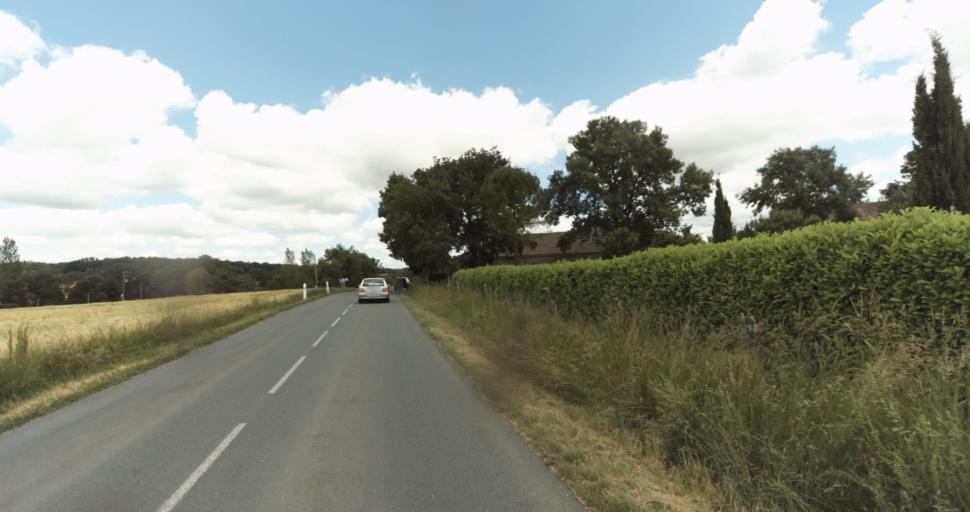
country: FR
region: Aquitaine
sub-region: Departement de la Dordogne
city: Beaumont-du-Perigord
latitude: 44.7160
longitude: 0.7508
